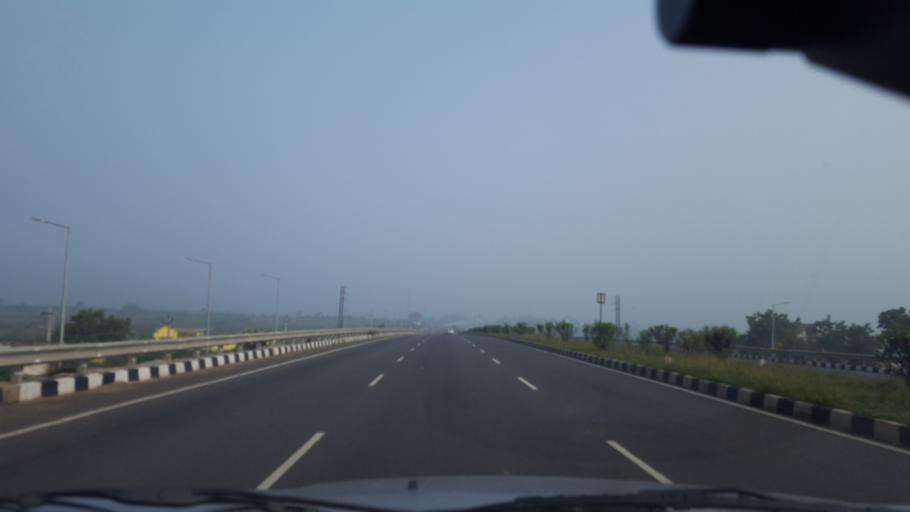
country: IN
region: Andhra Pradesh
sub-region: Prakasam
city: Ongole
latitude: 15.4138
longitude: 80.0392
